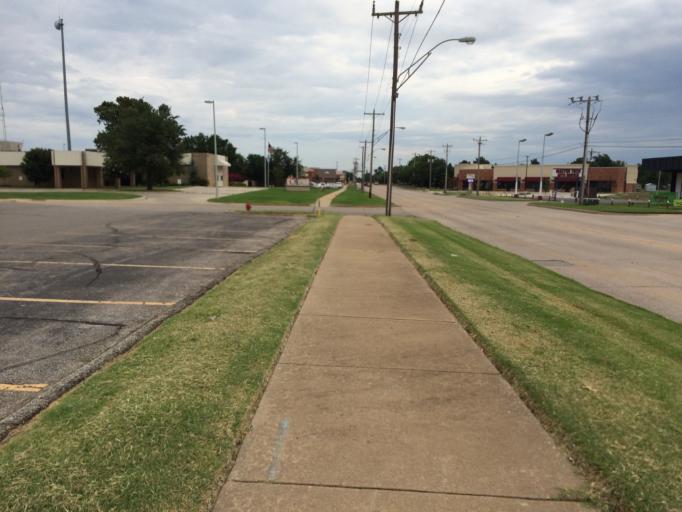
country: US
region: Oklahoma
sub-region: Cleveland County
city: Norman
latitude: 35.2205
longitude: -97.4768
